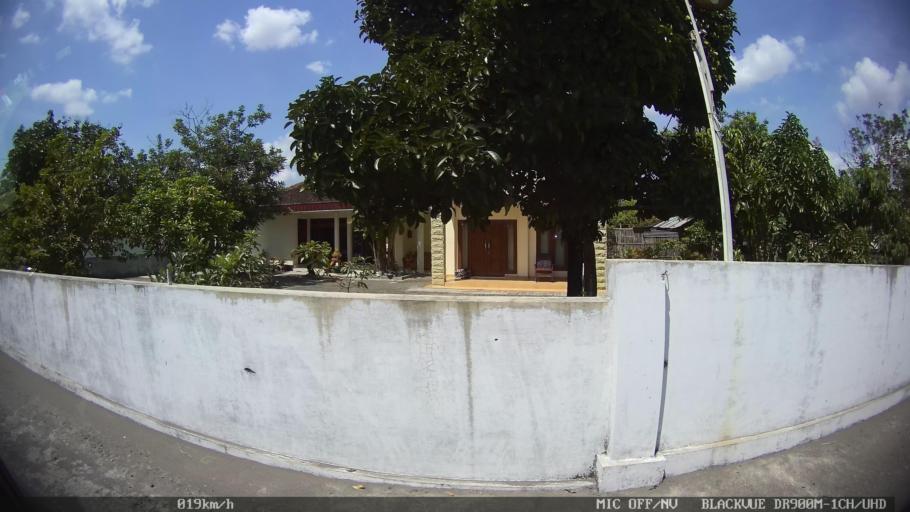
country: ID
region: Daerah Istimewa Yogyakarta
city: Sewon
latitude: -7.8475
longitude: 110.3857
